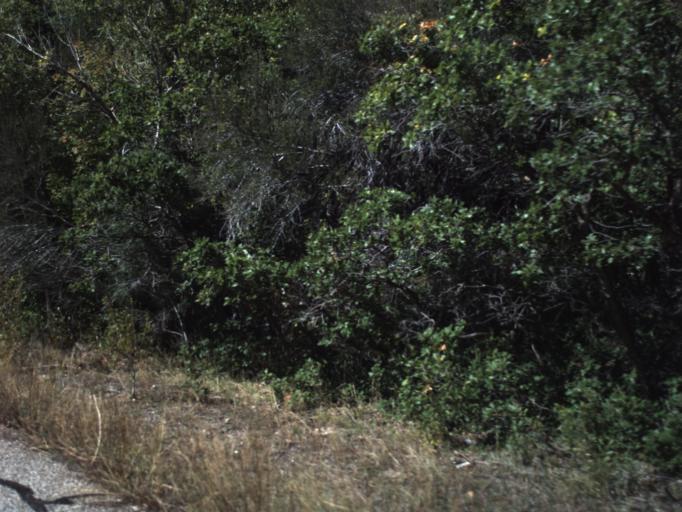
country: US
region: Utah
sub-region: Beaver County
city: Beaver
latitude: 38.2562
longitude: -112.5257
